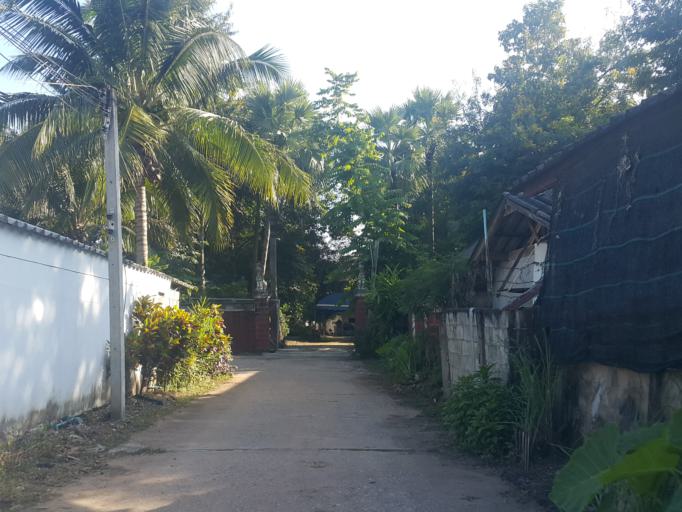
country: TH
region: Chiang Mai
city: Mae On
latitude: 18.7199
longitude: 99.2105
